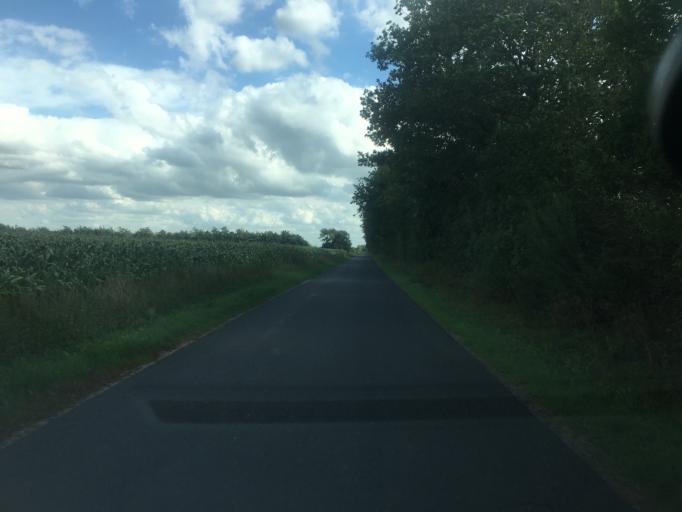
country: DK
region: South Denmark
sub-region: Tonder Kommune
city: Logumkloster
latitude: 55.0104
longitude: 9.0038
